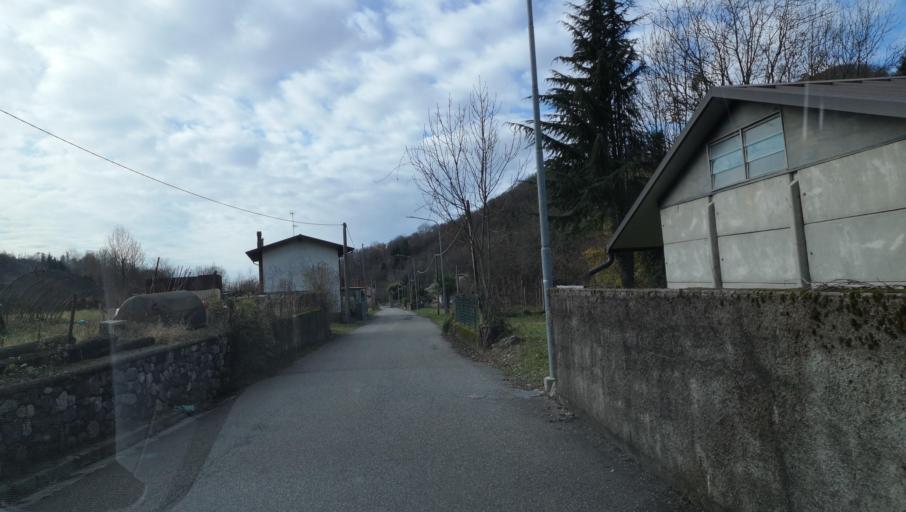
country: IT
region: Friuli Venezia Giulia
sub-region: Provincia di Udine
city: Attimis
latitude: 46.2159
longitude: 13.3159
